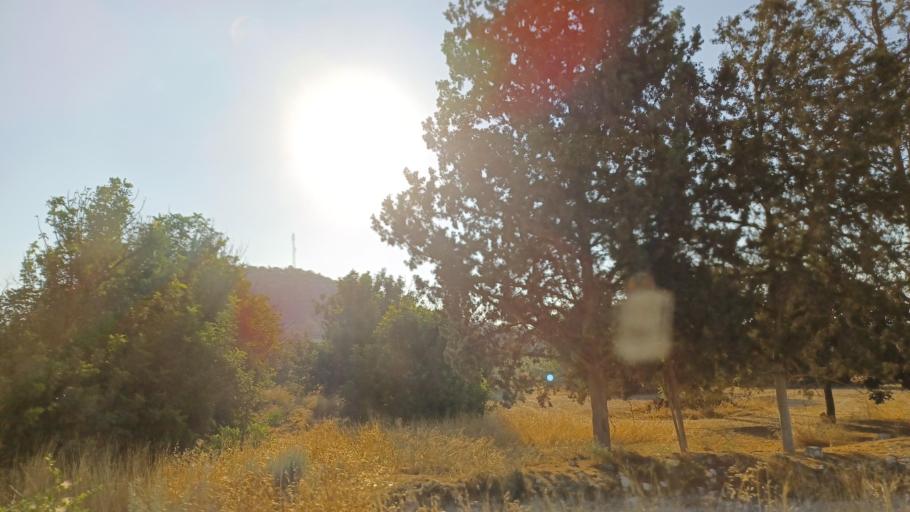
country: CY
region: Lefkosia
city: Lympia
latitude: 34.9797
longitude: 33.5148
